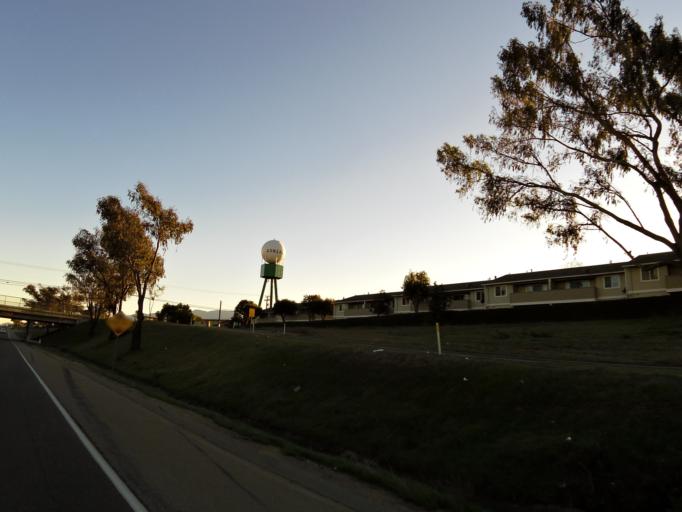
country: US
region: California
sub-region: Monterey County
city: Gonzales
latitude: 36.5143
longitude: -121.4383
